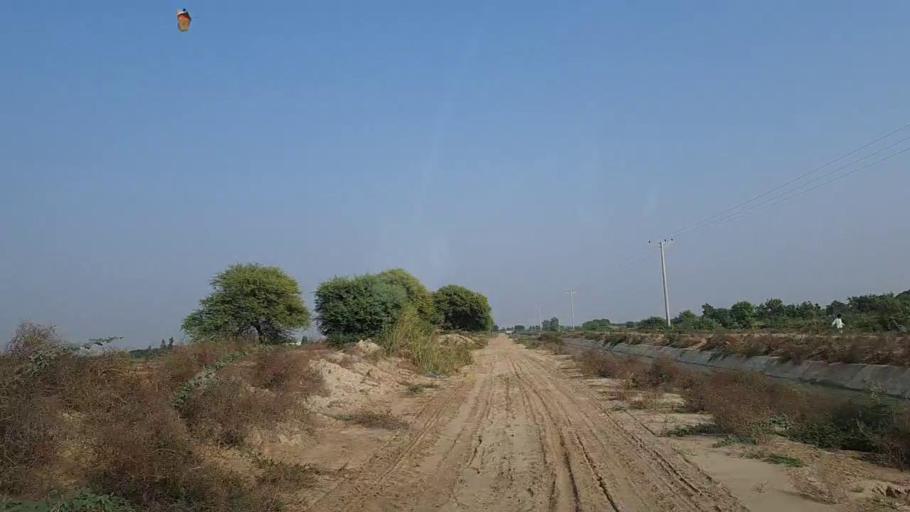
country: PK
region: Sindh
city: Mirpur Sakro
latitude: 24.6155
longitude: 67.7271
